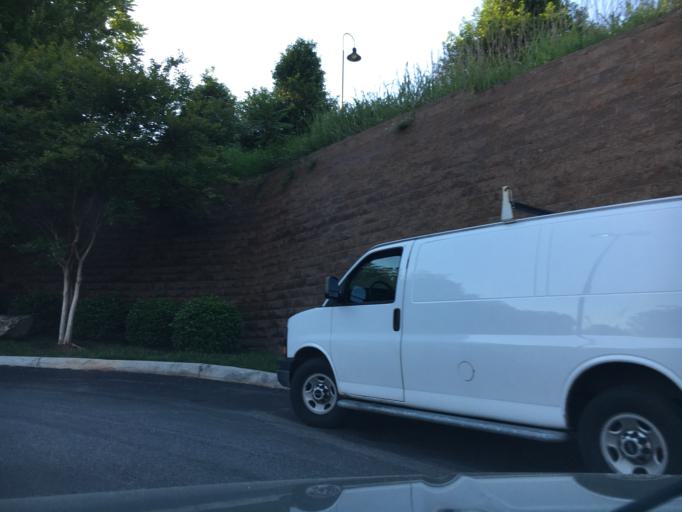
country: US
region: Virginia
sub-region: City of Lynchburg
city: West Lynchburg
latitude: 37.3562
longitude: -79.1846
